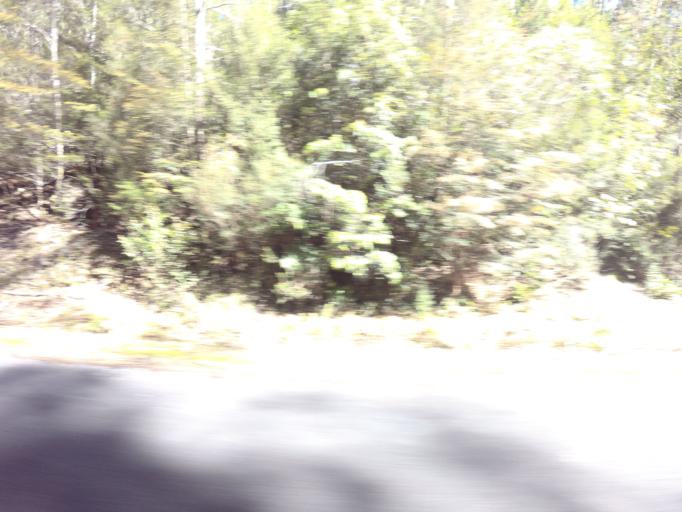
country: AU
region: Tasmania
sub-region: Huon Valley
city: Geeveston
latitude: -42.8277
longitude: 146.3209
